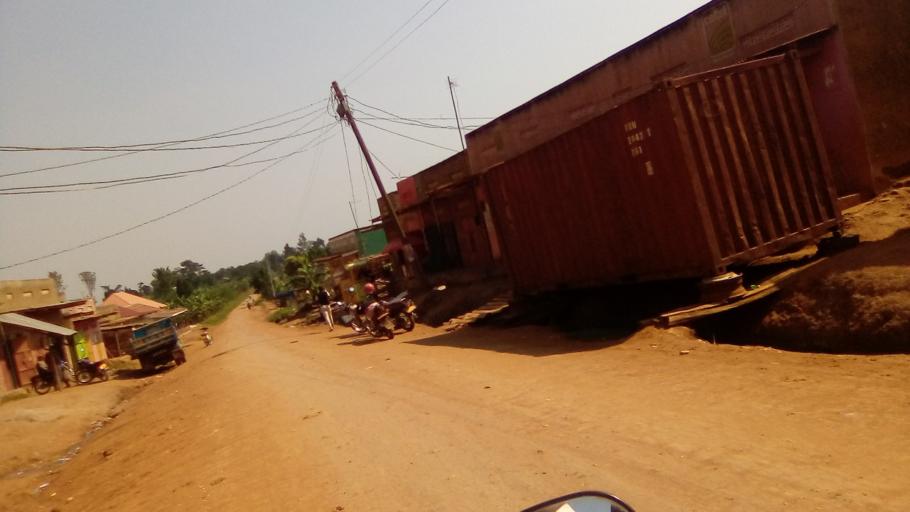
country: UG
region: Central Region
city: Masaka
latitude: -0.2683
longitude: 31.6473
